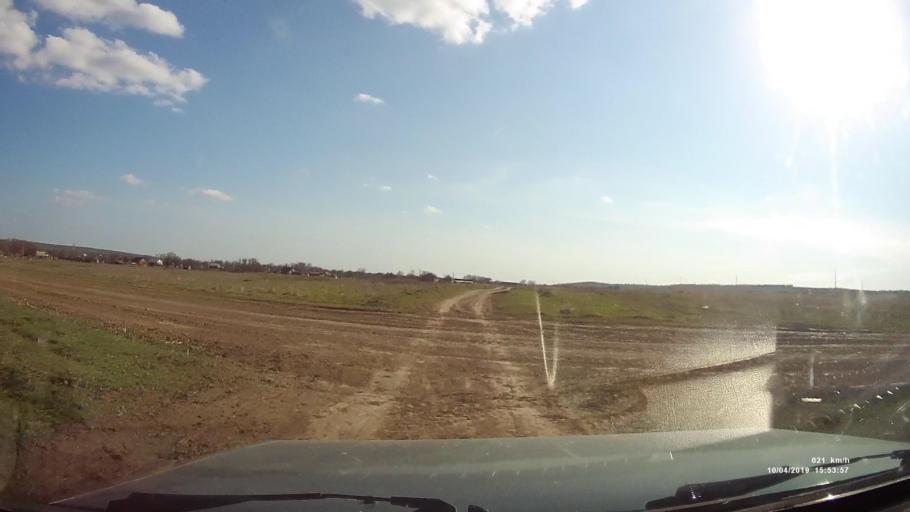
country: RU
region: Rostov
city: Masalovka
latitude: 48.4150
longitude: 40.2583
